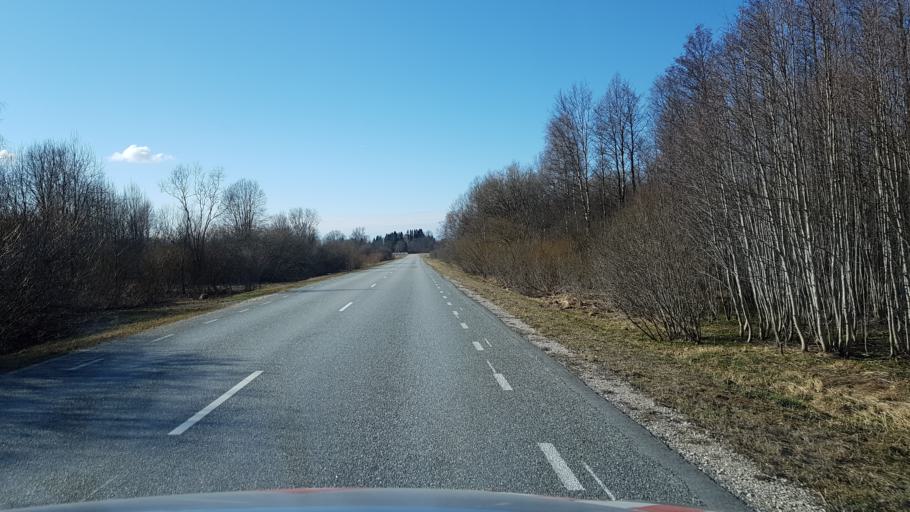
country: EE
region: Laeaene-Virumaa
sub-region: Haljala vald
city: Haljala
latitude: 59.5061
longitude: 26.1166
